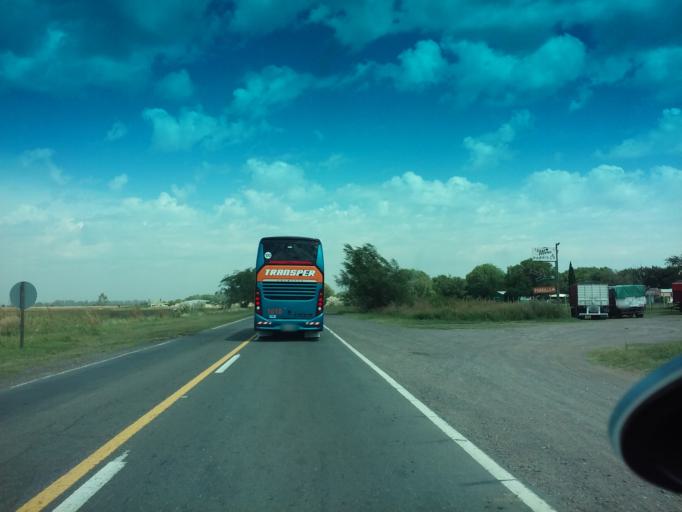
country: AR
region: Buenos Aires
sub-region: Partido de Carlos Casares
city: Carlos Casares
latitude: -35.6431
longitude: -61.3675
